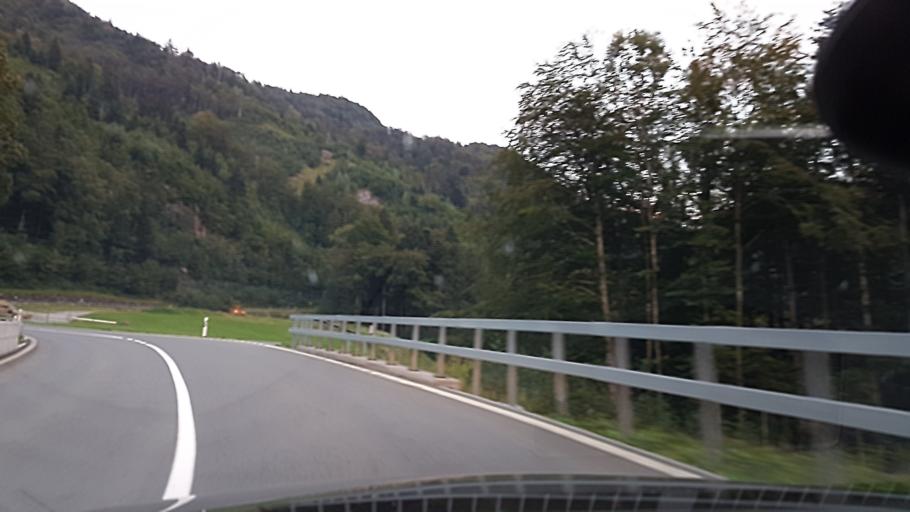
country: CH
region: Obwalden
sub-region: Obwalden
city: Engelberg
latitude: 46.8473
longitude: 8.3735
